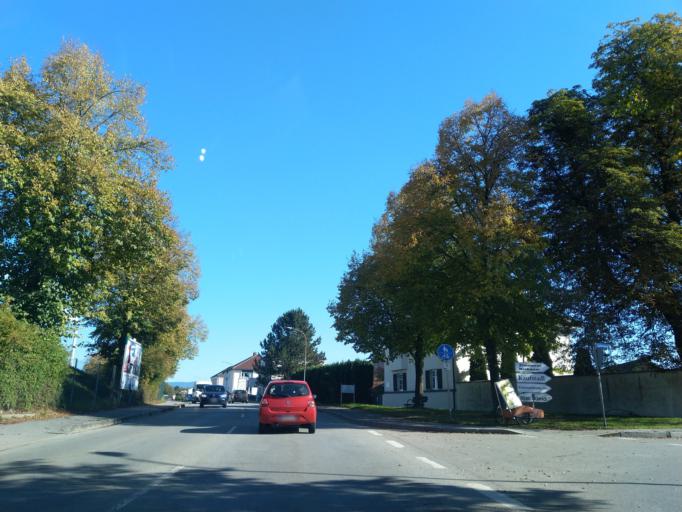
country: DE
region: Bavaria
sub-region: Lower Bavaria
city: Plattling
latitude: 48.7783
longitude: 12.8768
